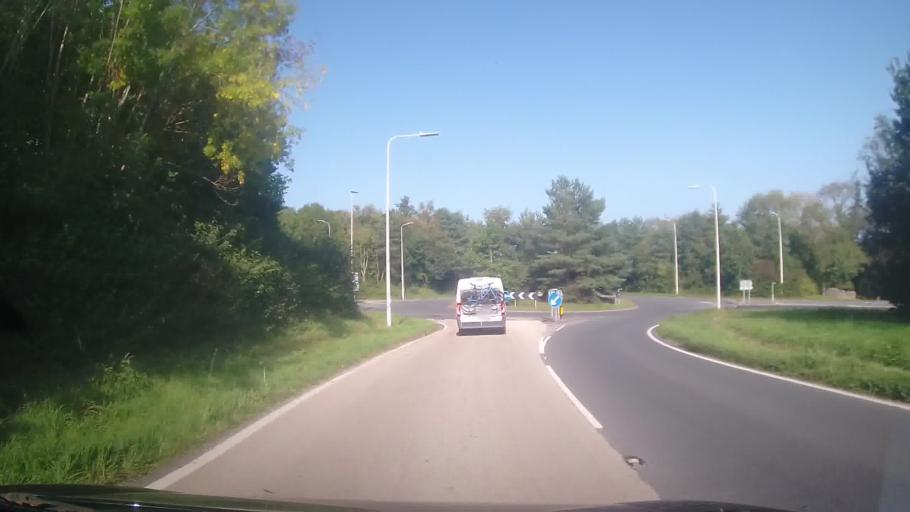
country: GB
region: Wales
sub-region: County of Ceredigion
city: Cardigan
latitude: 52.0757
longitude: -4.6568
